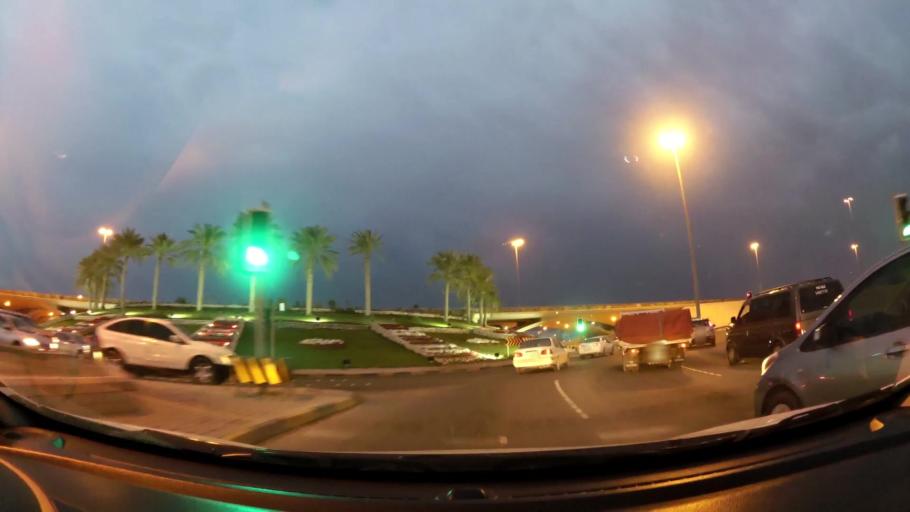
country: BH
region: Central Governorate
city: Madinat Hamad
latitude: 26.1395
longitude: 50.5098
